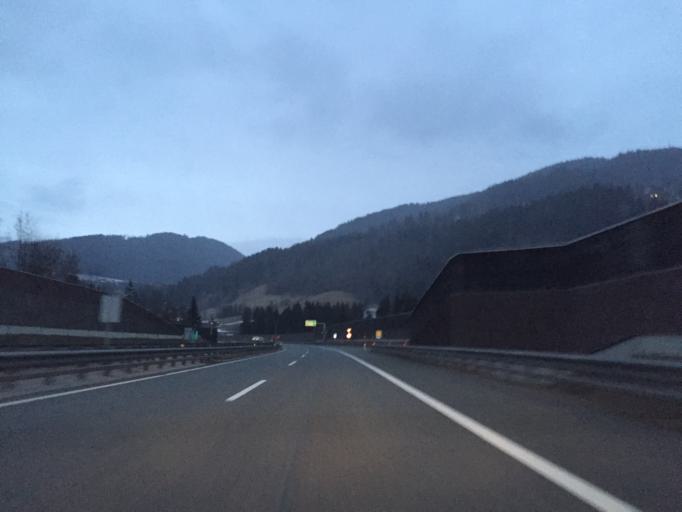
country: AT
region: Salzburg
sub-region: Politischer Bezirk Sankt Johann im Pongau
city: Eben im Pongau
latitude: 47.4153
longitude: 13.3881
